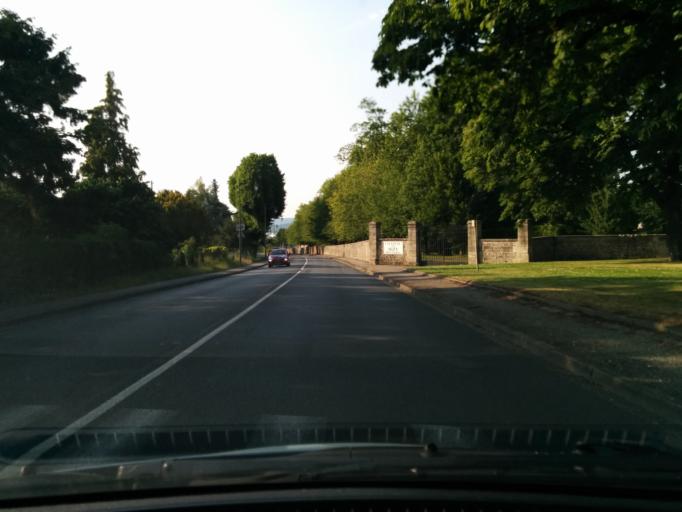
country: FR
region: Haute-Normandie
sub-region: Departement de l'Eure
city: Vernon
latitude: 49.0816
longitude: 1.4641
